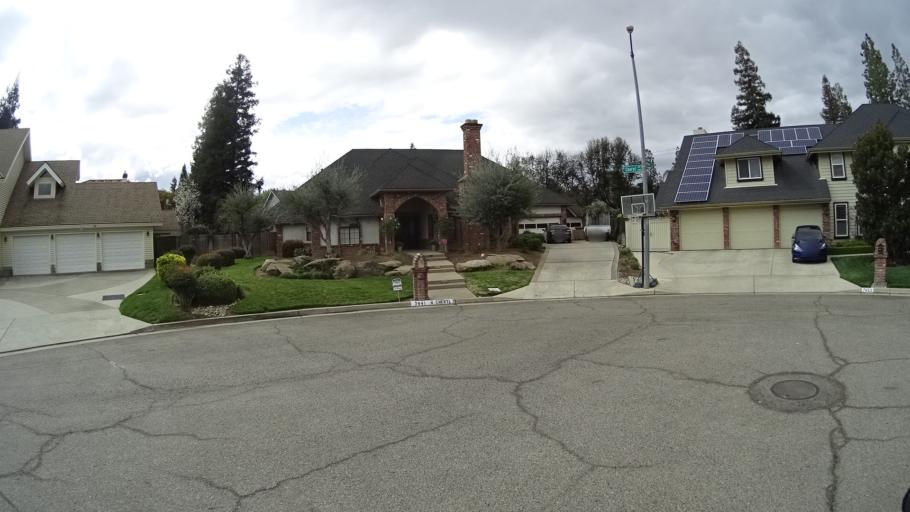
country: US
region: California
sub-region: Fresno County
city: Fresno
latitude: 36.8452
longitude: -119.8469
